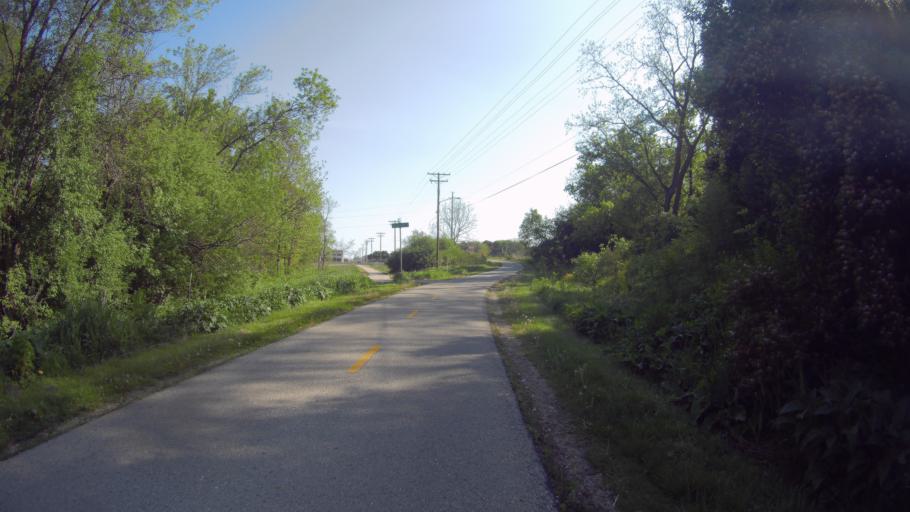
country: US
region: Wisconsin
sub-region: Dane County
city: Shorewood Hills
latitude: 43.0415
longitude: -89.4583
